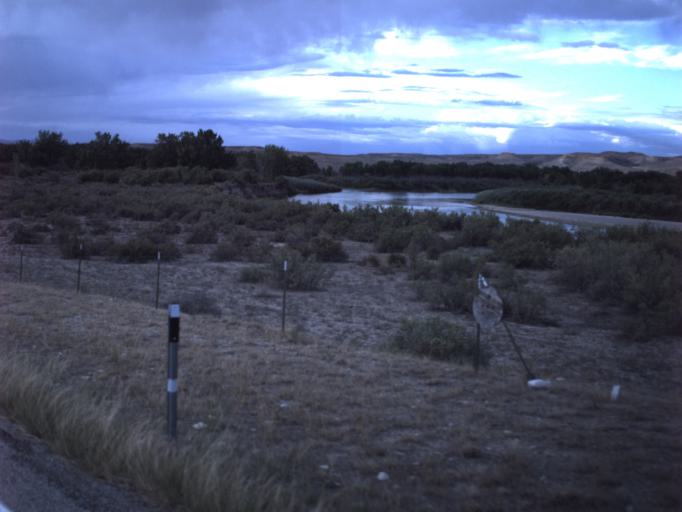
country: US
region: Utah
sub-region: Grand County
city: Moab
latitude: 38.8513
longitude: -109.2852
